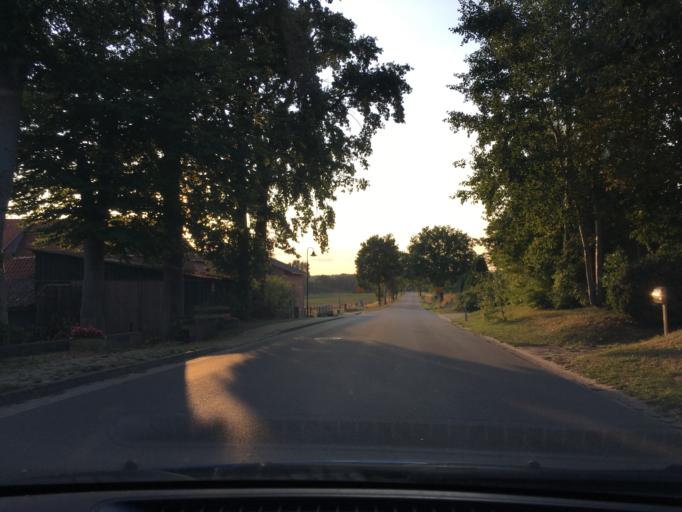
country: DE
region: Lower Saxony
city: Bleckede
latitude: 53.2569
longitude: 10.7577
